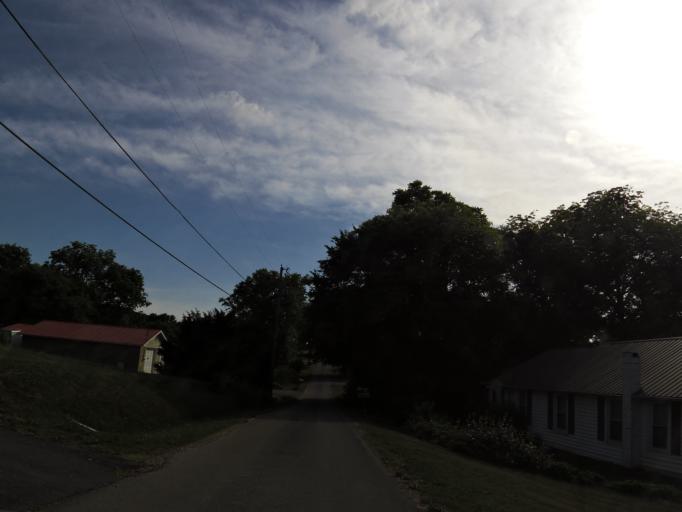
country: US
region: Tennessee
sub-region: Blount County
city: Eagleton Village
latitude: 35.8236
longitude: -83.9477
